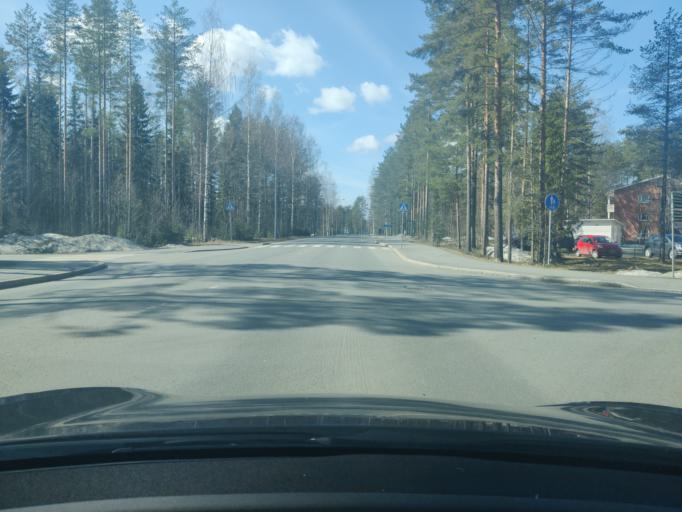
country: FI
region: Northern Savo
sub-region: Kuopio
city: Vehmersalmi
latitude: 62.9139
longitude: 28.1540
